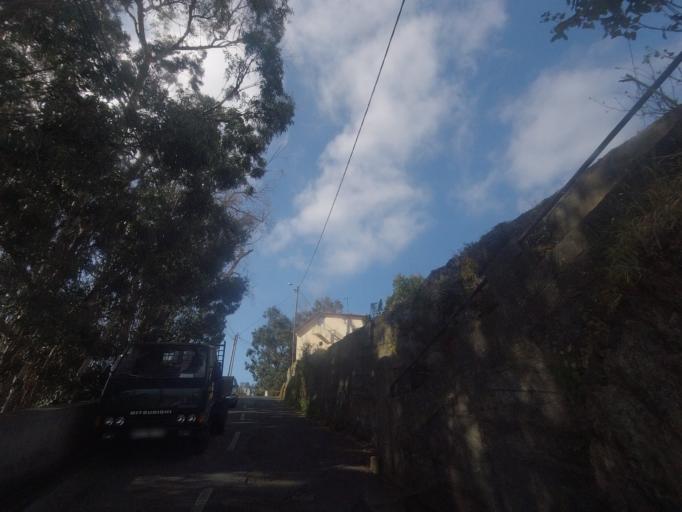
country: PT
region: Madeira
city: Camara de Lobos
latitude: 32.6761
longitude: -16.9539
